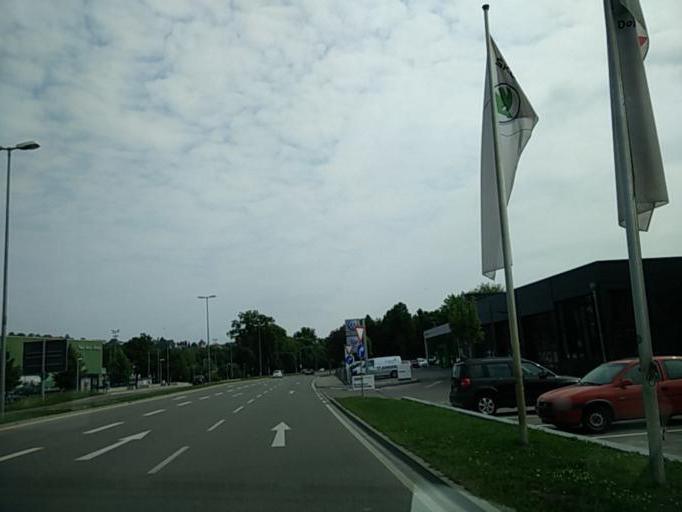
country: DE
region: Baden-Wuerttemberg
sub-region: Tuebingen Region
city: Tuebingen
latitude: 48.5094
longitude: 9.0423
